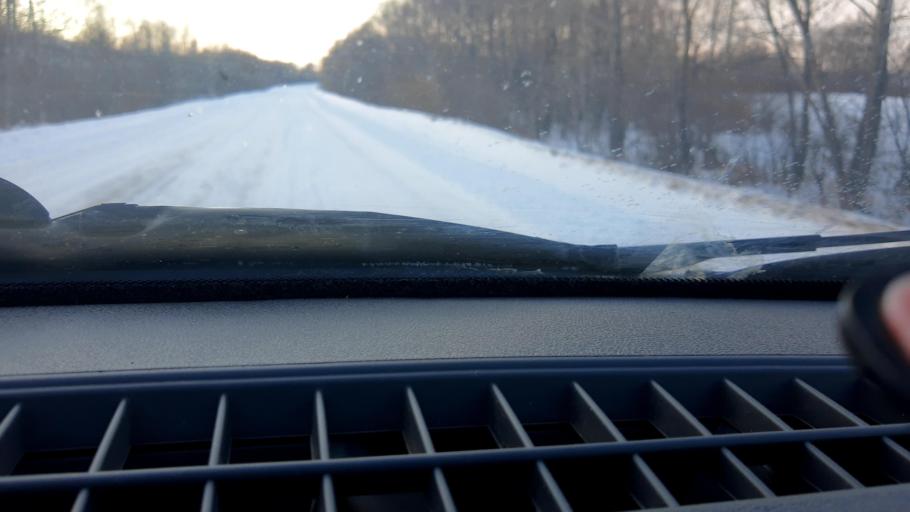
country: RU
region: Bashkortostan
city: Kushnarenkovo
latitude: 55.1394
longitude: 55.6279
